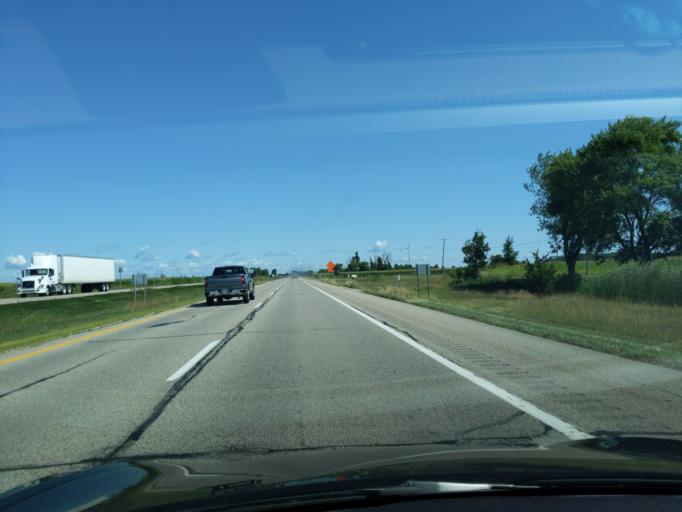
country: US
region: Michigan
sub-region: Gratiot County
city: Ithaca
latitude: 43.2541
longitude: -84.5631
